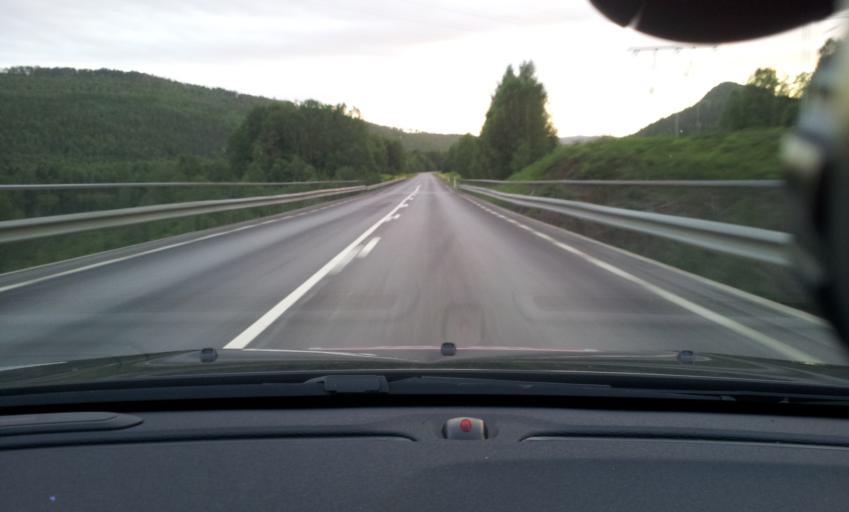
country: SE
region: Jaemtland
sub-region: Ragunda Kommun
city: Hammarstrand
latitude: 63.0928
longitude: 16.4486
